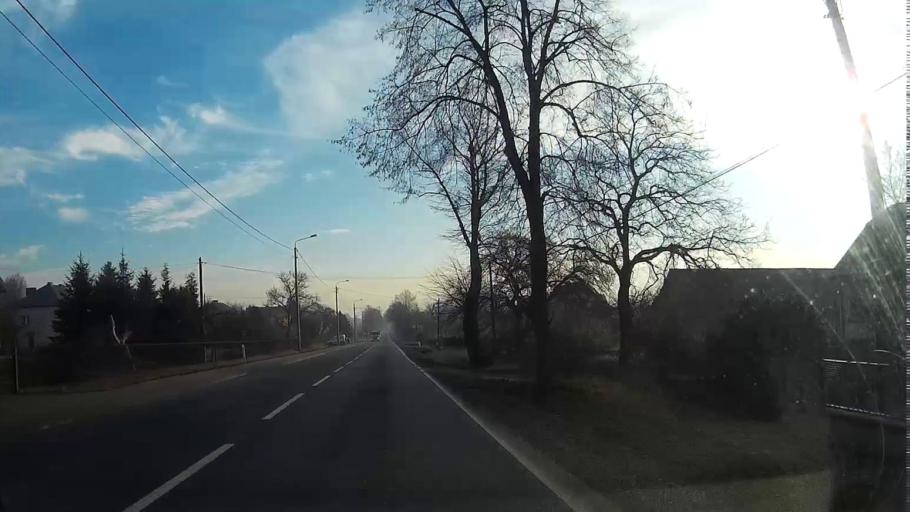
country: PL
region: Lesser Poland Voivodeship
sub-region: Powiat chrzanowski
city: Babice
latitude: 50.0700
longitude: 19.4596
